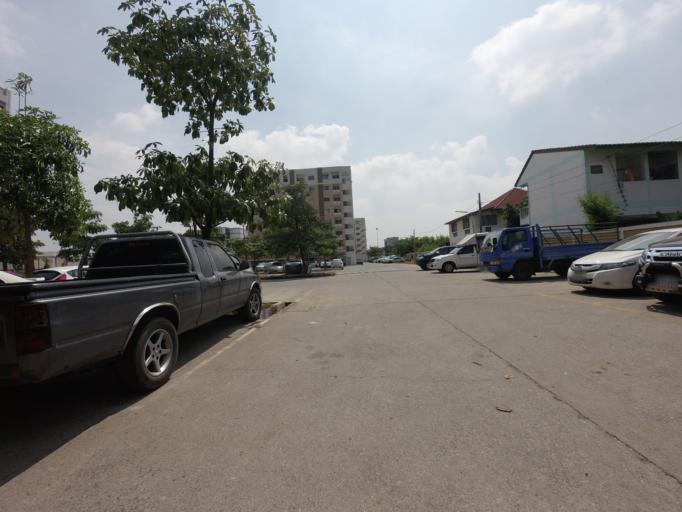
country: TH
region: Bangkok
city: Bueng Kum
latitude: 13.7844
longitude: 100.6819
